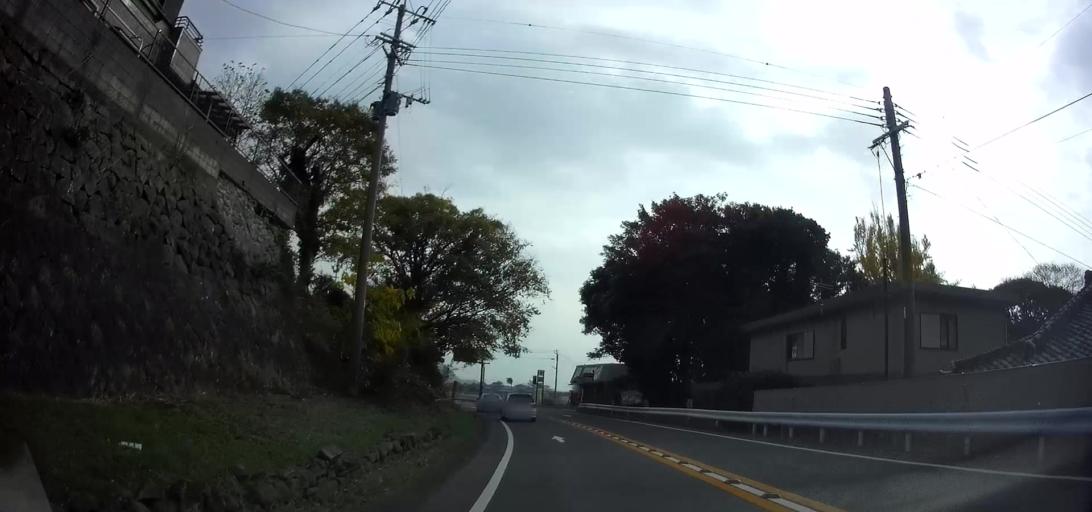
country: JP
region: Nagasaki
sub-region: Isahaya-shi
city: Isahaya
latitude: 32.7962
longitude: 130.1366
